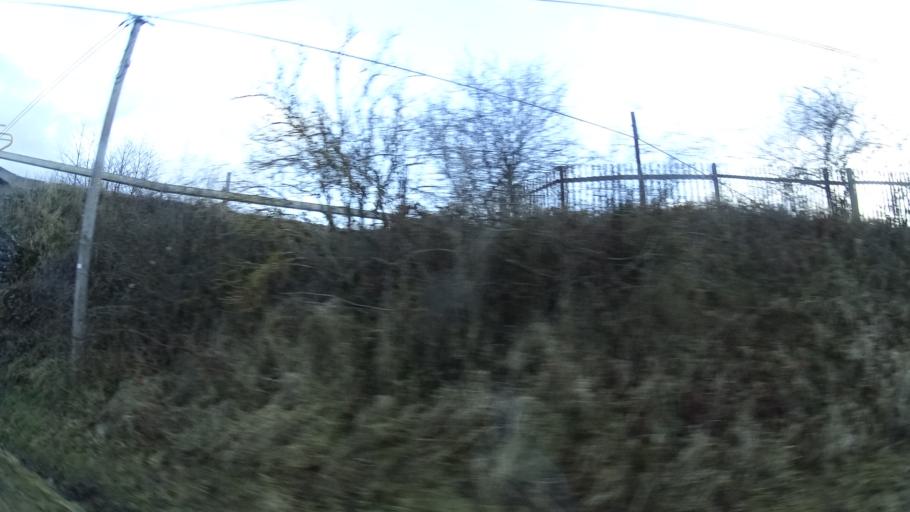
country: DE
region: Thuringia
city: Stadtilm
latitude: 50.7313
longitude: 11.0651
